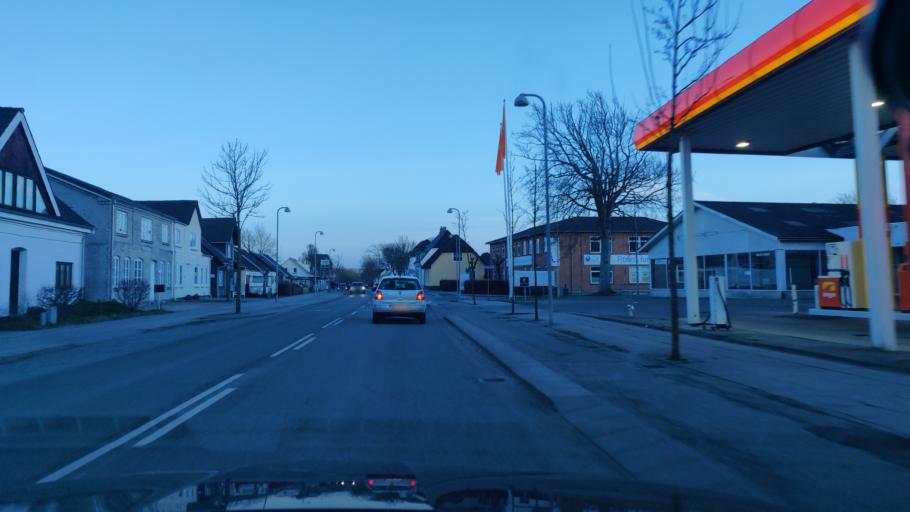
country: DK
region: North Denmark
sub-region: Alborg Kommune
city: Aalborg
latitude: 57.0661
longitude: 9.9039
